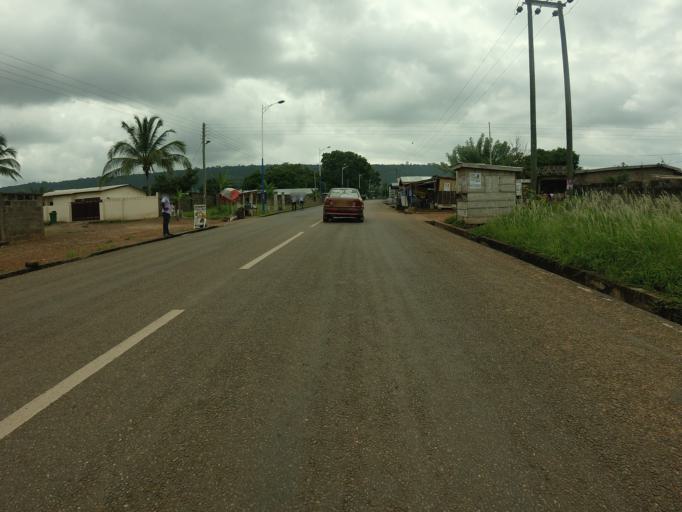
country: GH
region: Volta
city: Ho
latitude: 6.6299
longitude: 0.4876
